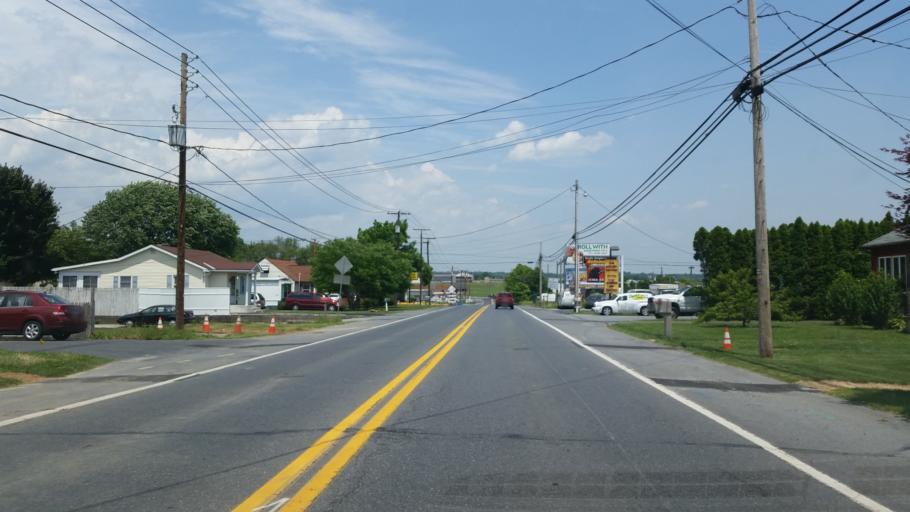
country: US
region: Pennsylvania
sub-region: Cumberland County
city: New Cumberland
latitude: 40.2145
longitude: -76.8638
